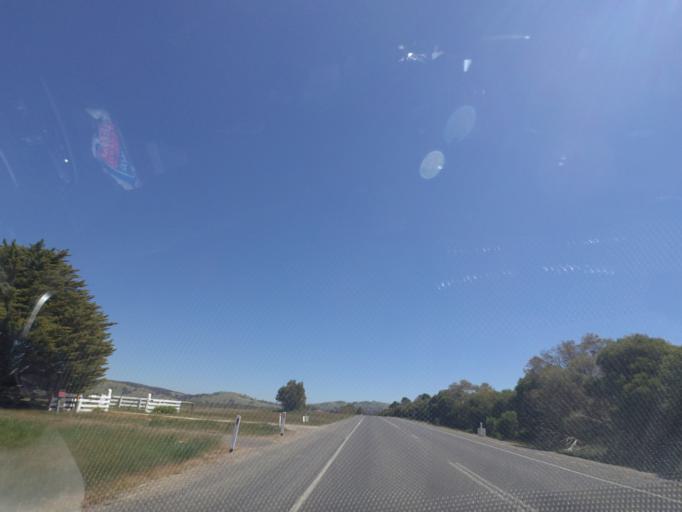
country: AU
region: Victoria
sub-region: Hume
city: Sunbury
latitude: -37.3088
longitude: 144.8422
